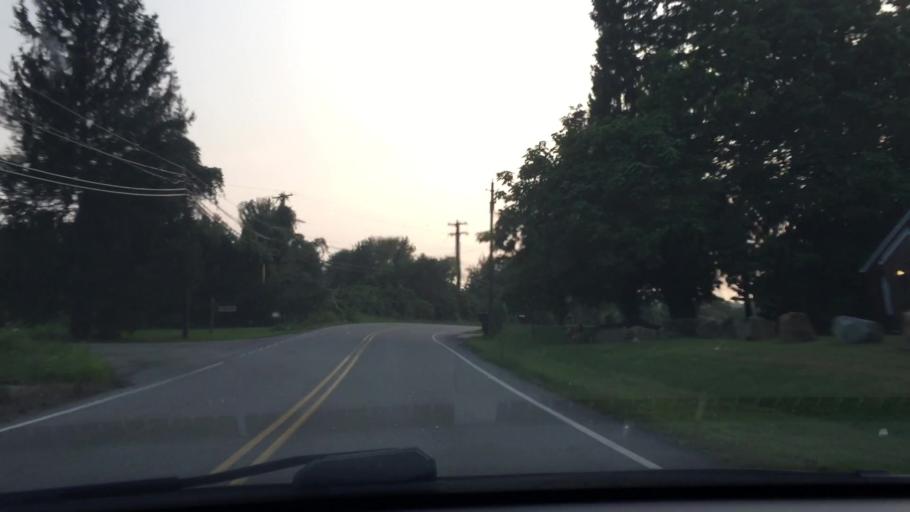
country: US
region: Pennsylvania
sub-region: Westmoreland County
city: Fellsburg
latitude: 40.1682
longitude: -79.8141
